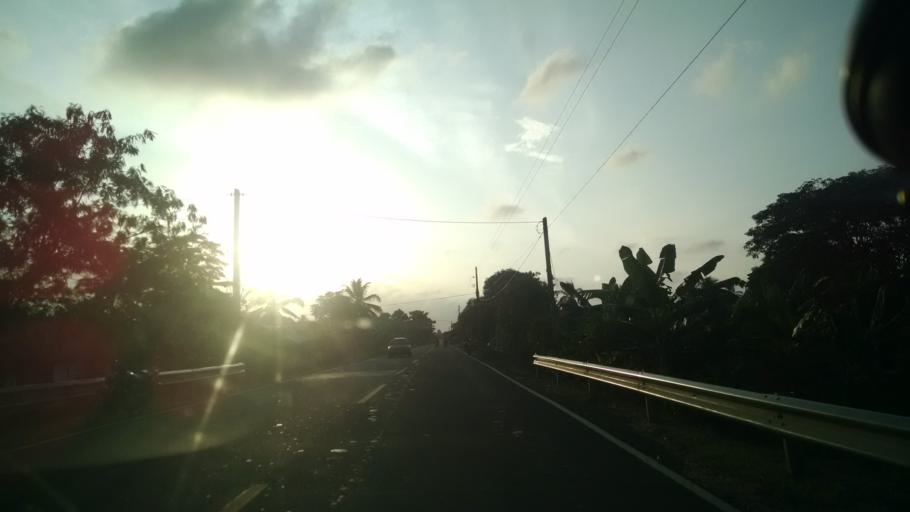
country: CO
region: Antioquia
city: San Juan de Uraba
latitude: 8.7341
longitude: -76.5727
